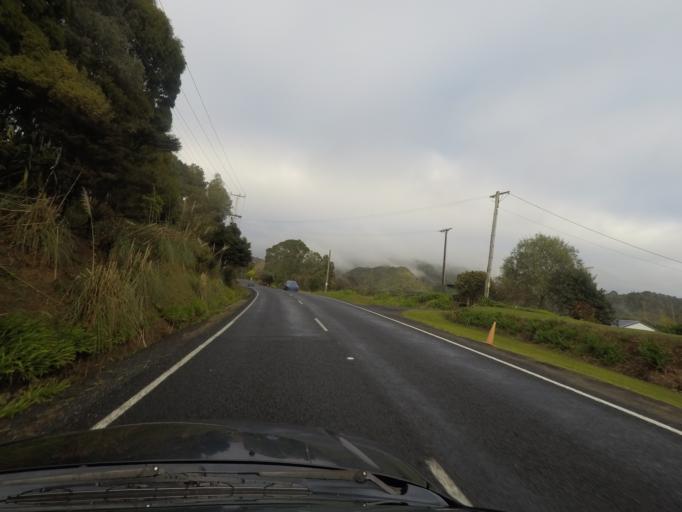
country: NZ
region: Auckland
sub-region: Auckland
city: Waitakere
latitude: -36.9187
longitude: 174.5871
